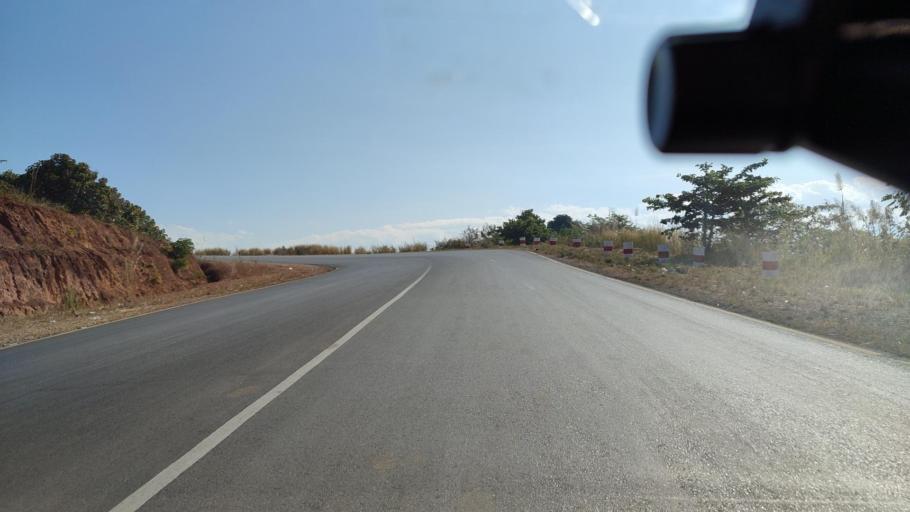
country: MM
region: Shan
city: Lashio
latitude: 23.3248
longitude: 97.9791
